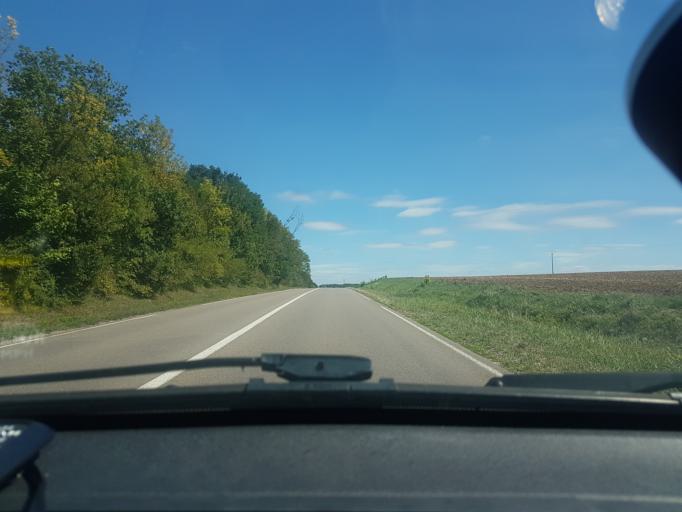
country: FR
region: Bourgogne
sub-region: Departement de la Cote-d'Or
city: Mirebeau-sur-Beze
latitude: 47.4023
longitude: 5.3321
